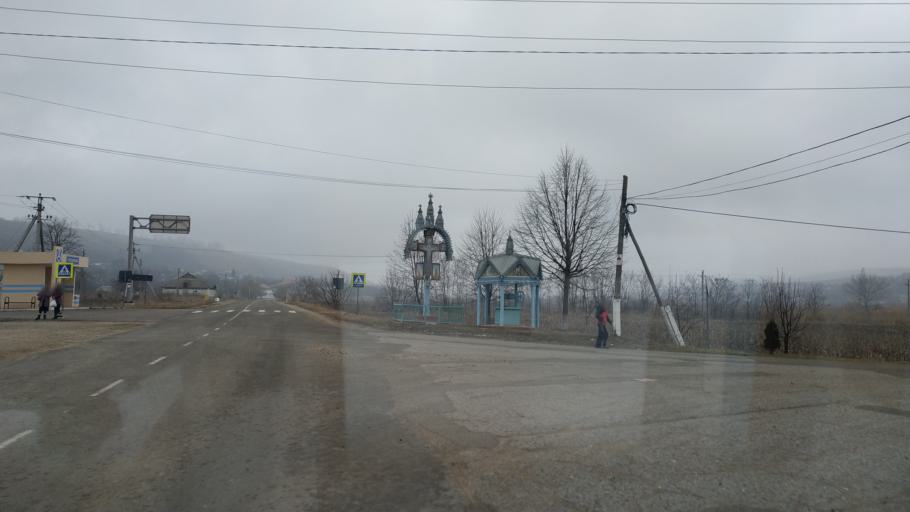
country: MD
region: Hincesti
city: Hincesti
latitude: 46.9558
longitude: 28.4926
